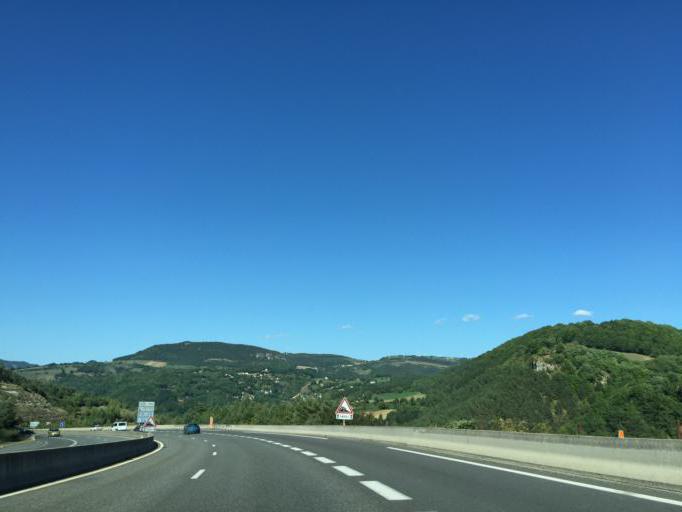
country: FR
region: Languedoc-Roussillon
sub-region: Departement de la Lozere
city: La Canourgue
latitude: 44.4246
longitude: 3.1856
